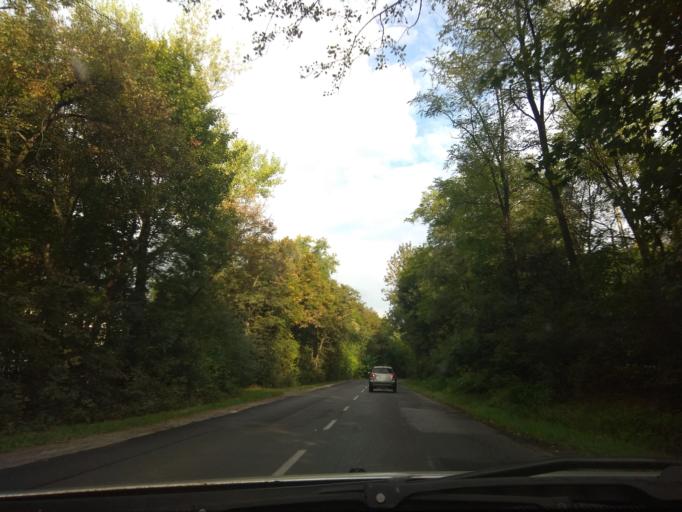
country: HU
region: Borsod-Abauj-Zemplen
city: Miskolc
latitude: 48.0826
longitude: 20.7707
